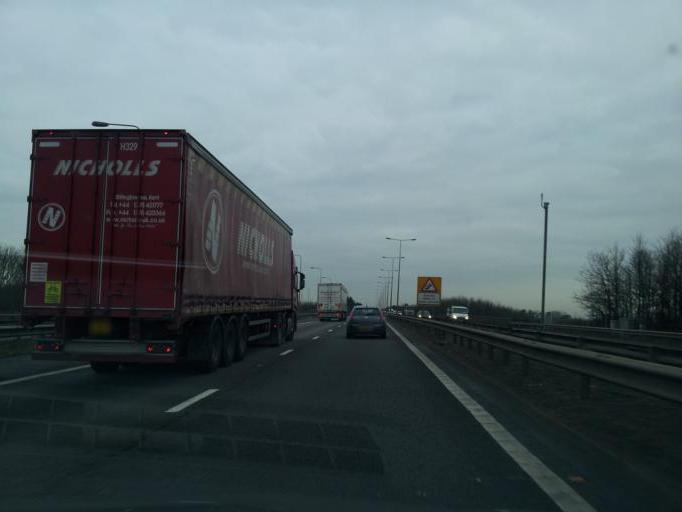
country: GB
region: England
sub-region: Cambridgeshire
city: Girton
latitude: 52.2298
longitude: 0.0718
